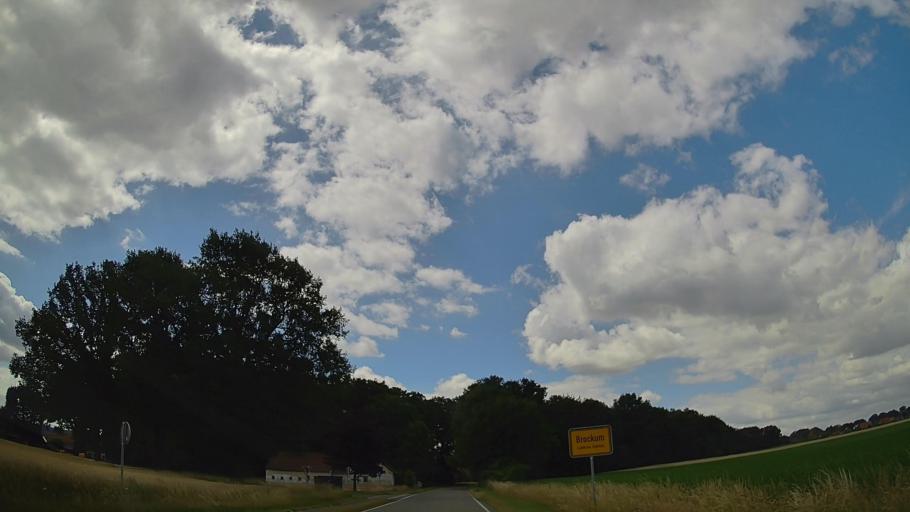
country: DE
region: Lower Saxony
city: Brockum
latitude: 52.4736
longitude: 8.4297
